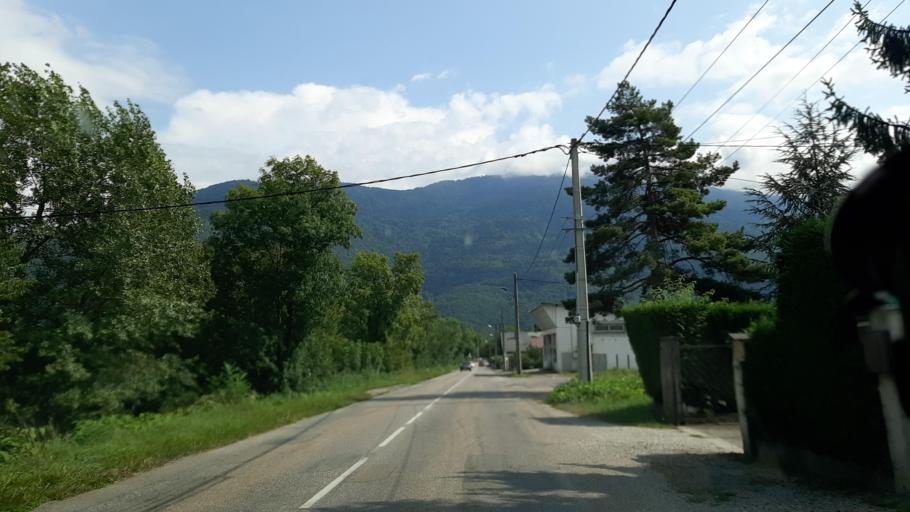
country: FR
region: Rhone-Alpes
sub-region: Departement de la Savoie
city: Gilly-sur-Isere
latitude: 45.6642
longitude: 6.3581
